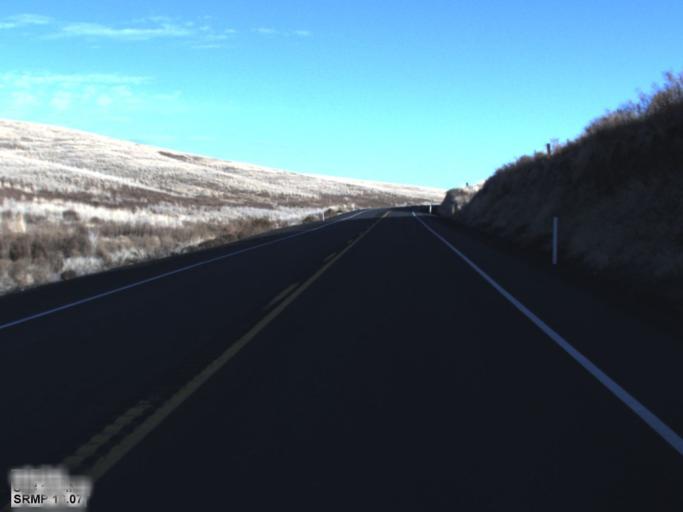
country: US
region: Washington
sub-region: Garfield County
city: Pomeroy
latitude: 46.6957
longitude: -117.7909
